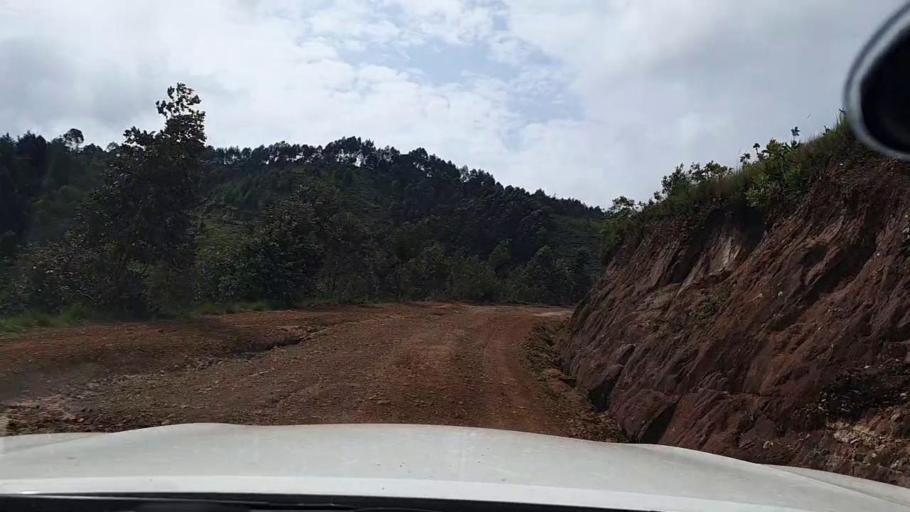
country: RW
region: Western Province
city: Kibuye
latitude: -2.1370
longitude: 29.3765
